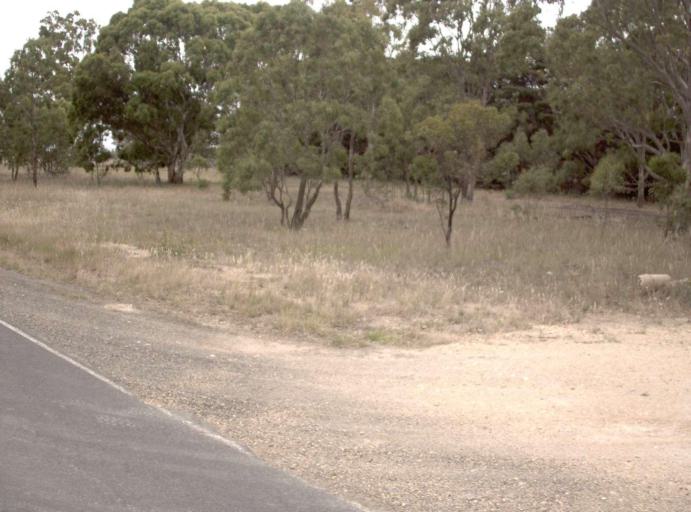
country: AU
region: Victoria
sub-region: Wellington
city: Heyfield
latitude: -38.0461
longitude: 146.7676
